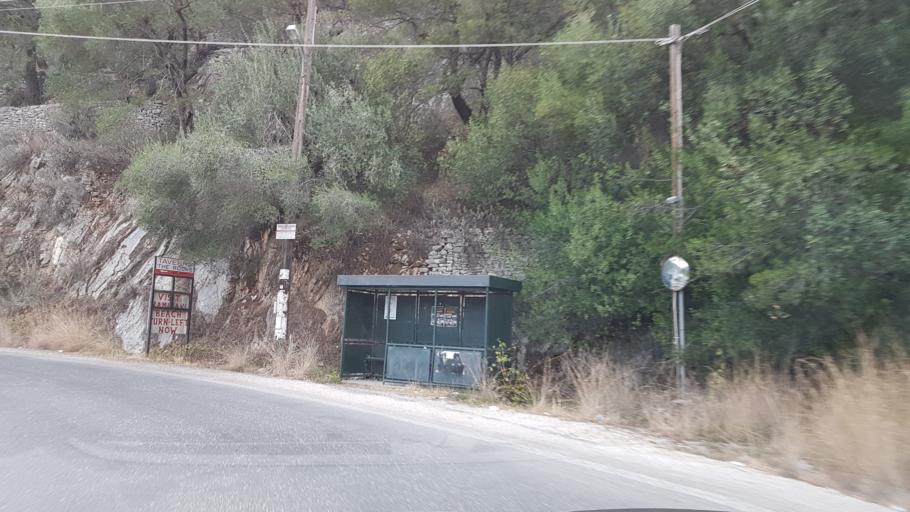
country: GR
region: Ionian Islands
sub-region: Nomos Kerkyras
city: Kontokali
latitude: 39.7307
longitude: 19.9110
